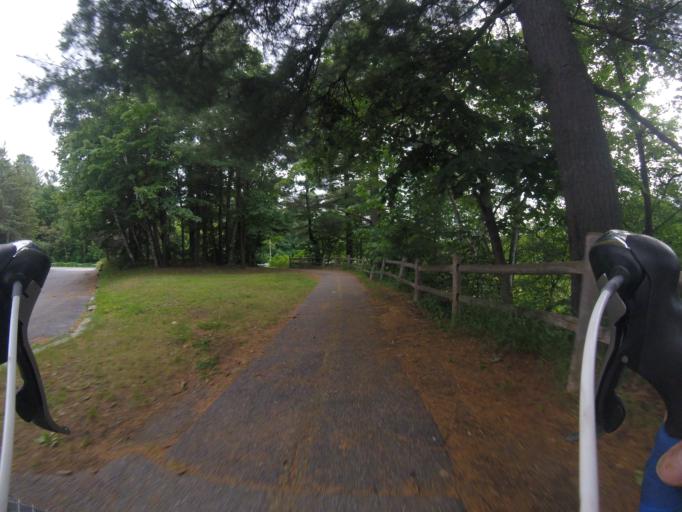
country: CA
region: Ontario
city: Bells Corners
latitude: 45.3258
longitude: -75.7853
